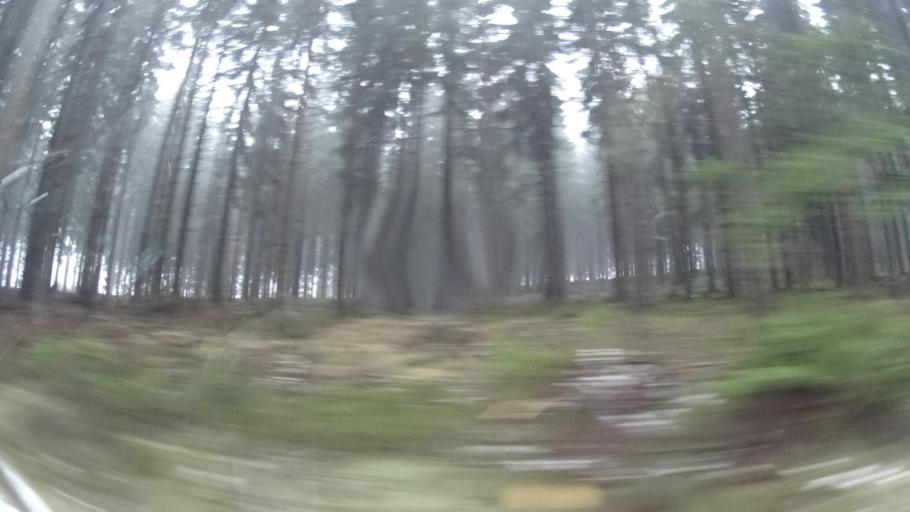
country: DE
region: Thuringia
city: Eisfeld
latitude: 50.5037
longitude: 10.9041
